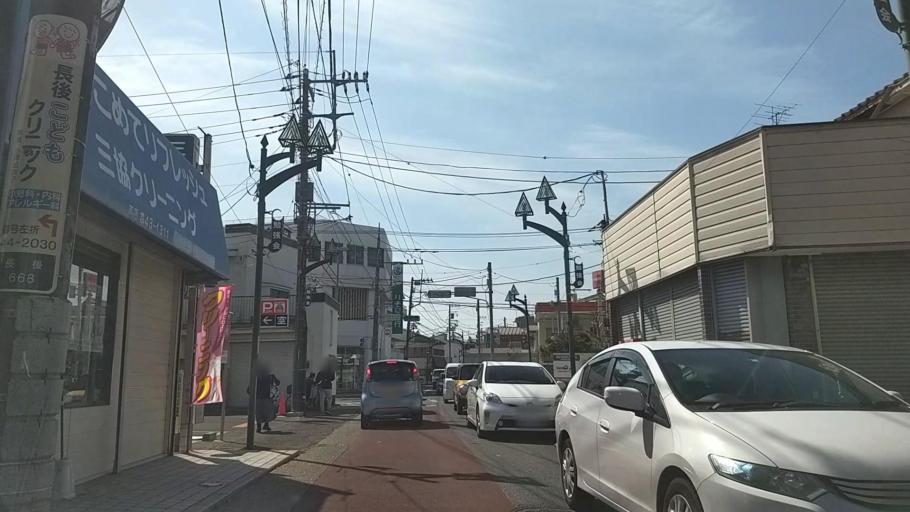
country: JP
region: Kanagawa
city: Minami-rinkan
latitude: 35.4135
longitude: 139.4650
